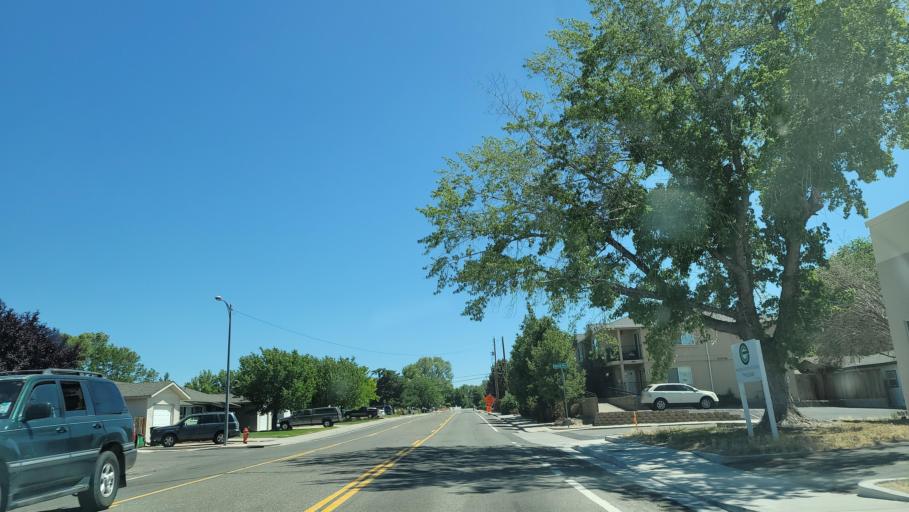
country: US
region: Nevada
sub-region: Carson City
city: Carson City
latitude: 39.1495
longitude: -119.7628
